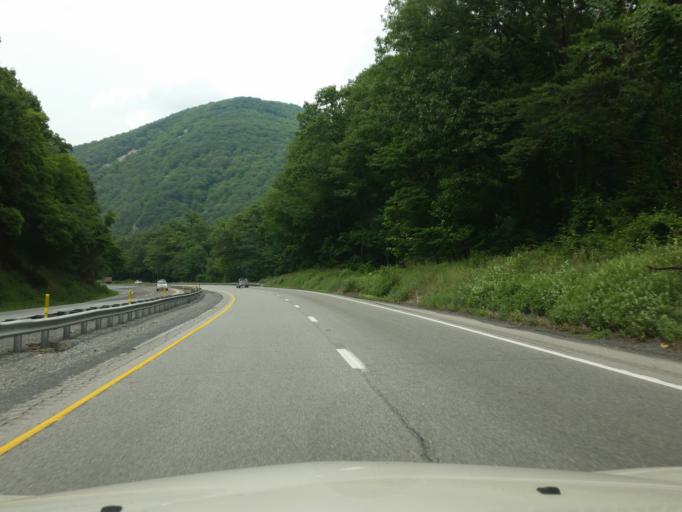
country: US
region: Pennsylvania
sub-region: Mifflin County
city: Yeagertown
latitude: 40.6462
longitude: -77.5829
